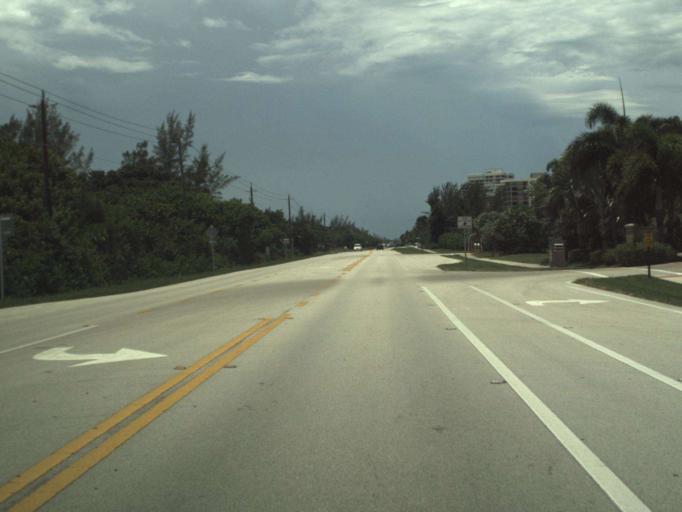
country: US
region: Florida
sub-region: Saint Lucie County
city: Hutchinson Island South
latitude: 27.2756
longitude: -80.2073
